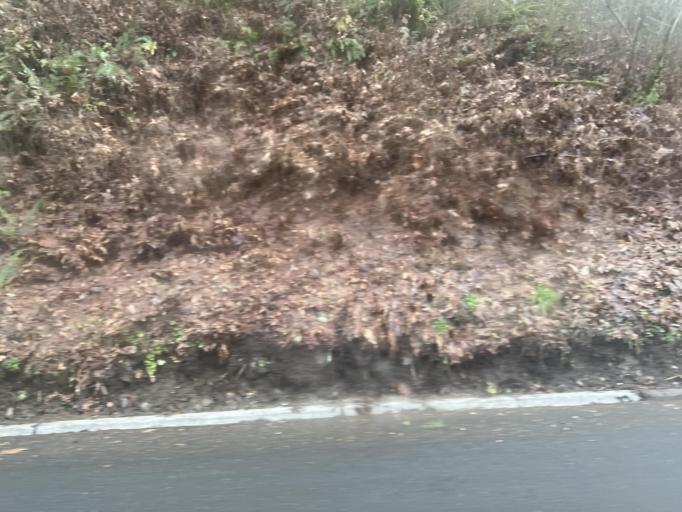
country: US
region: Washington
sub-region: Clark County
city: Washougal
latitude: 45.5332
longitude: -122.2342
